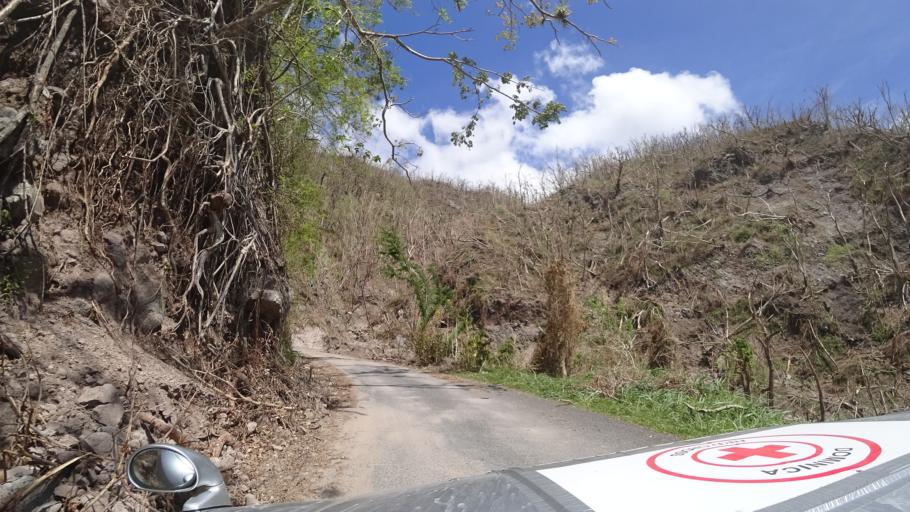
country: DM
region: Saint Mark
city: Soufriere
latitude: 15.2429
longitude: -61.3689
